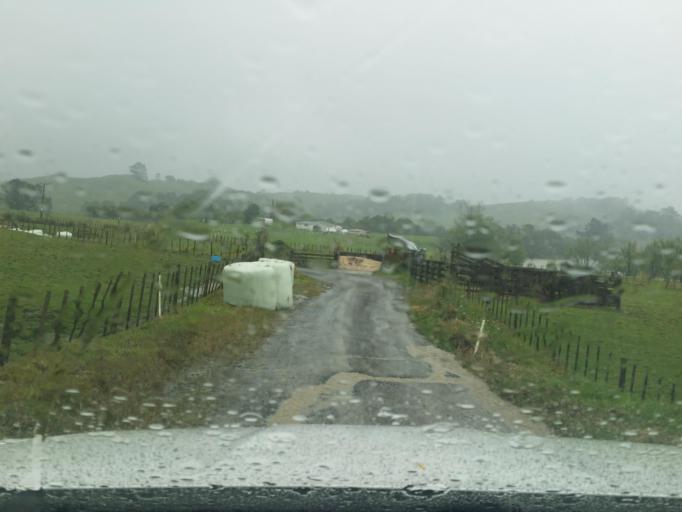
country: NZ
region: Northland
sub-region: Kaipara District
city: Dargaville
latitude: -35.8643
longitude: 174.0202
